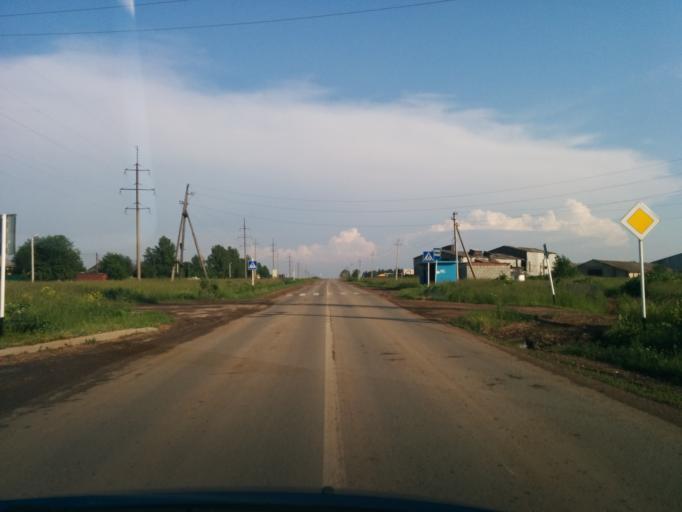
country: RU
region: Perm
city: Polazna
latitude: 58.2302
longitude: 56.2887
